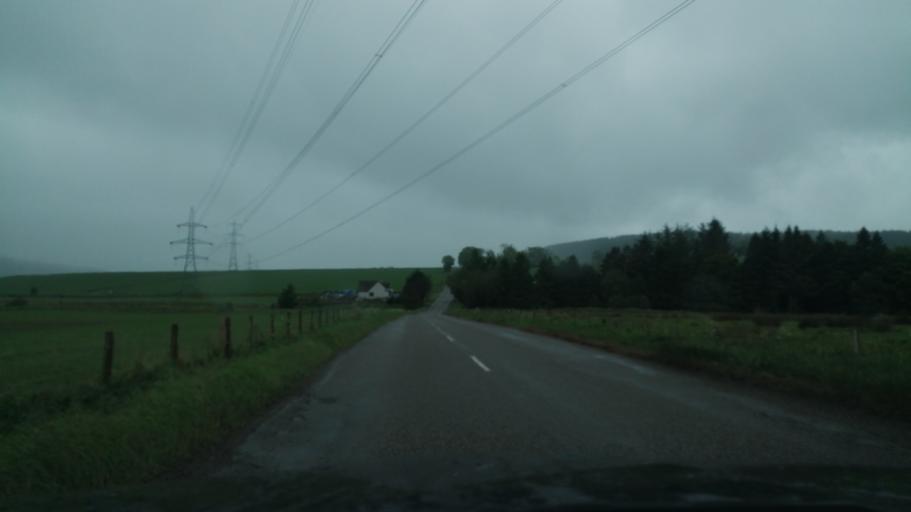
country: GB
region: Scotland
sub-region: Aberdeenshire
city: Huntly
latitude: 57.5443
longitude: -2.8055
